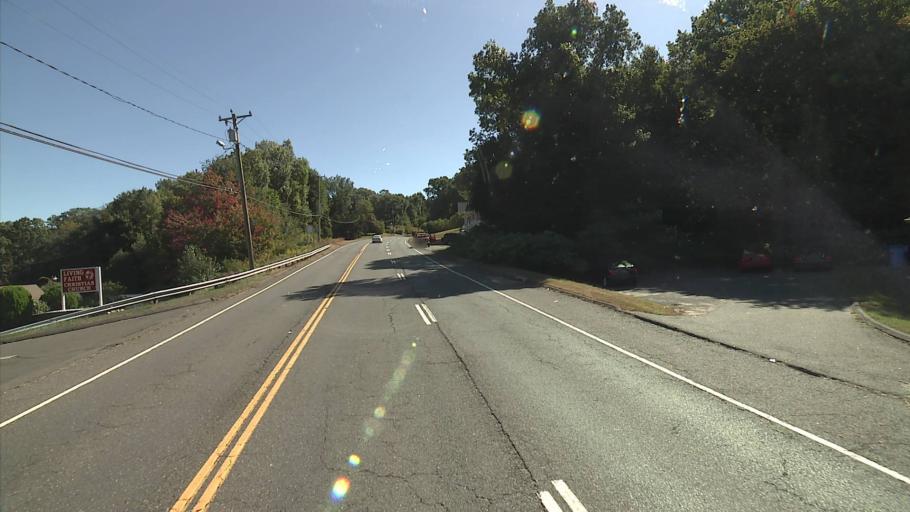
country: US
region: Connecticut
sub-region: New Haven County
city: Waterbury
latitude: 41.5366
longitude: -73.0145
